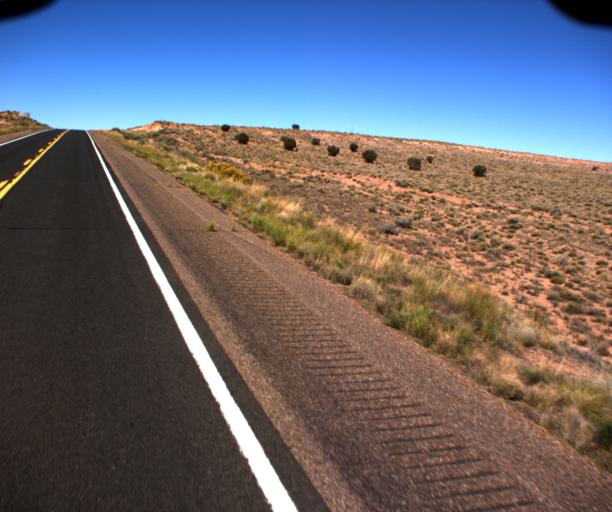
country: US
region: Arizona
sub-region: Navajo County
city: Snowflake
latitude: 34.6861
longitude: -109.7395
